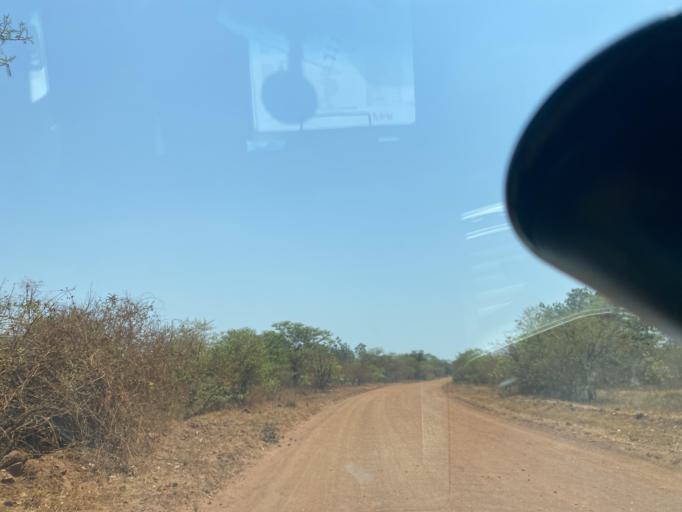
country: ZM
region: Southern
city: Nakambala
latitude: -15.4980
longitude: 27.9081
